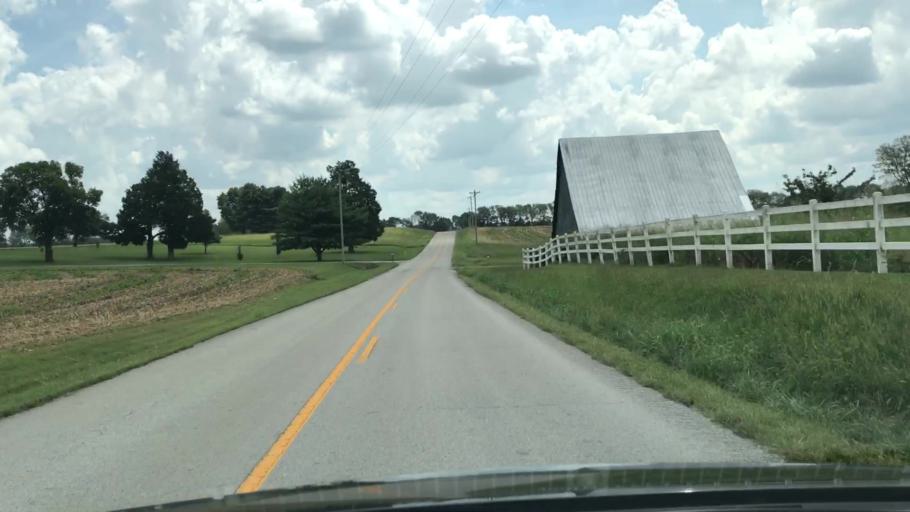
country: US
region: Kentucky
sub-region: Todd County
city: Elkton
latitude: 36.7865
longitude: -87.1308
